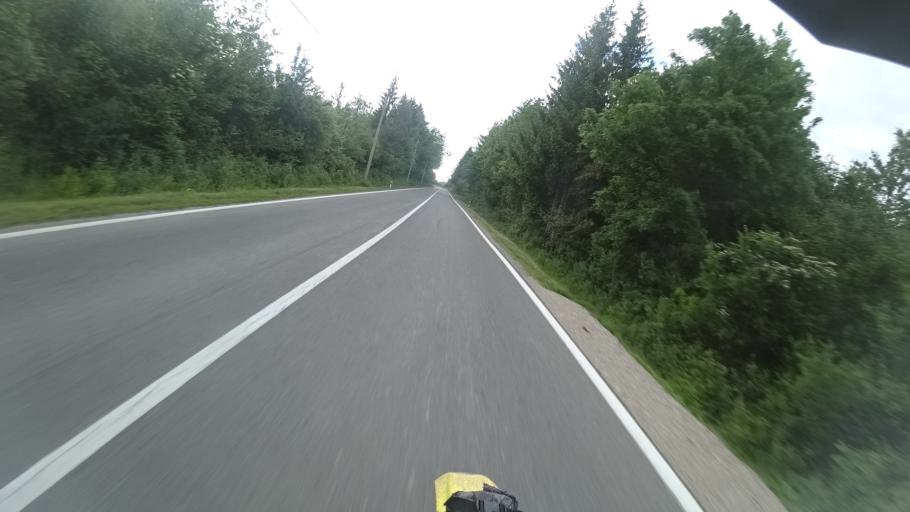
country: HR
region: Licko-Senjska
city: Gospic
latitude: 44.4952
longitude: 15.4596
